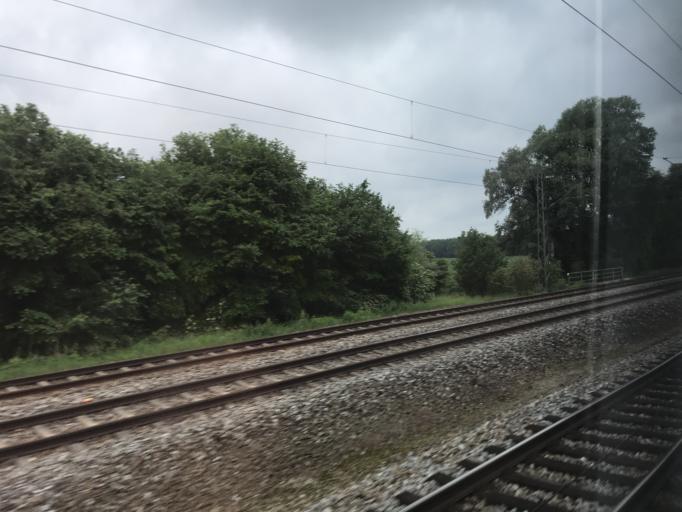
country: DE
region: Bavaria
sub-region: Upper Bavaria
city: Grobenzell
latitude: 48.1997
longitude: 11.3657
